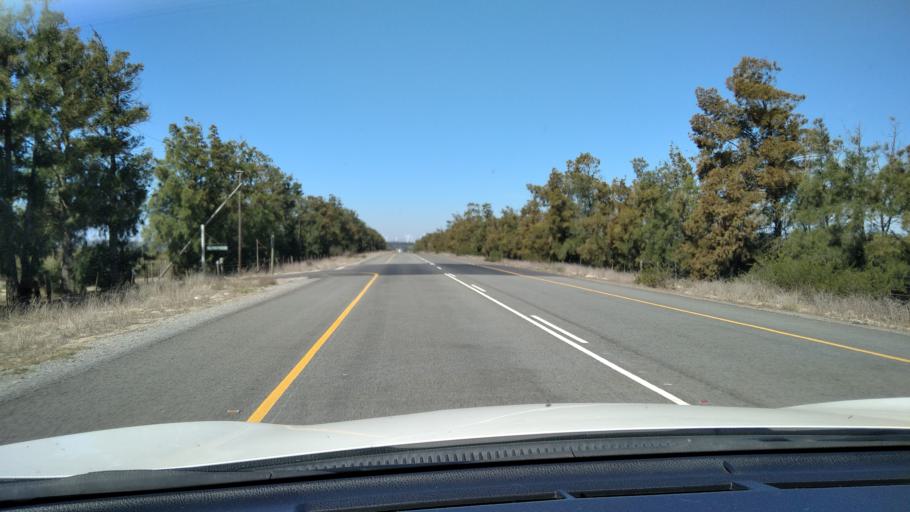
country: ZA
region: Western Cape
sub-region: West Coast District Municipality
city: Vredenburg
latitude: -33.0444
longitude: 18.3183
